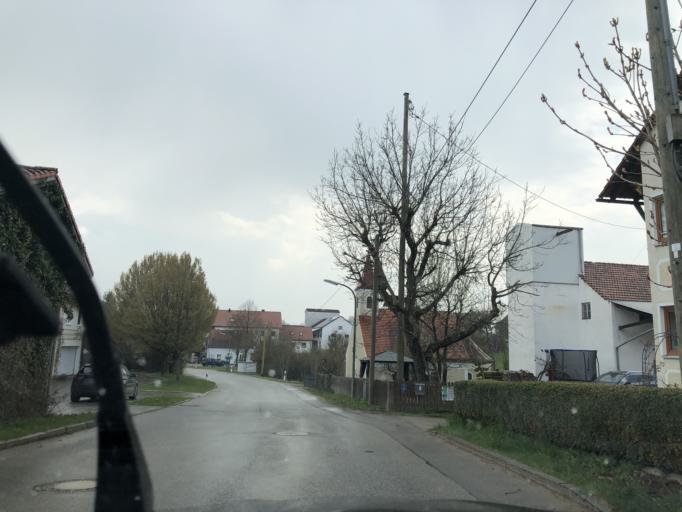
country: DE
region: Bavaria
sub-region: Upper Bavaria
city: Wolfersdorf
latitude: 48.5166
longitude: 11.6749
